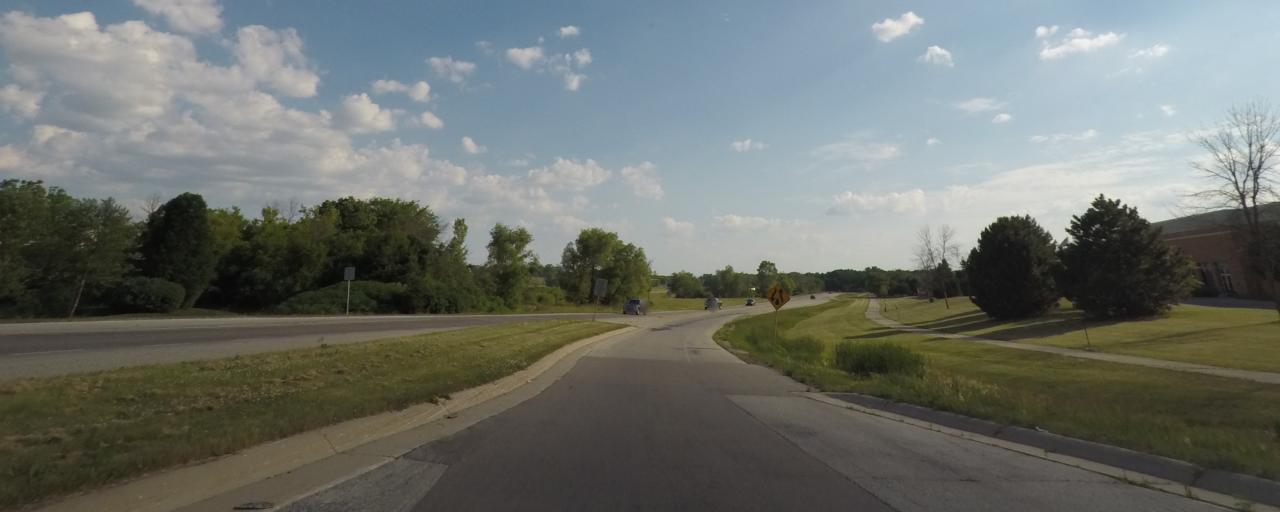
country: US
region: Wisconsin
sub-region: Waukesha County
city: New Berlin
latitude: 42.9419
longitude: -88.1091
